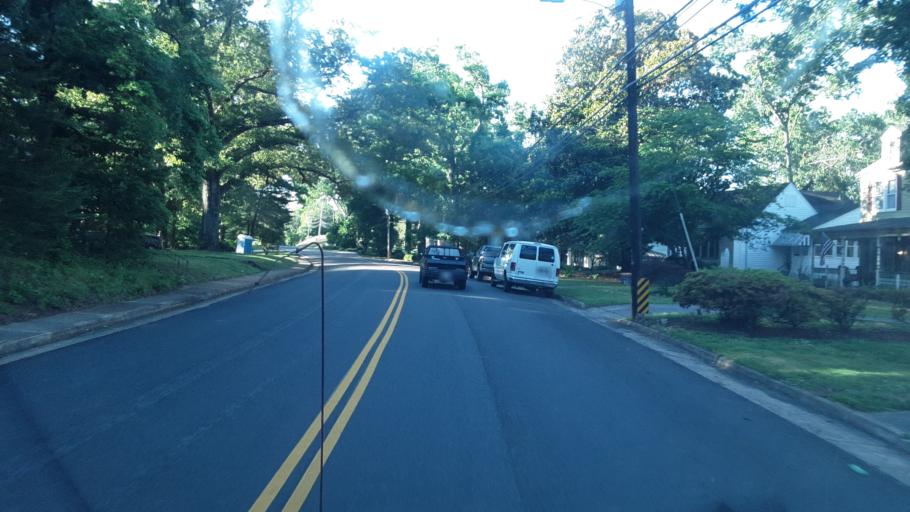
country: US
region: Virginia
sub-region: Pittsylvania County
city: Chatham
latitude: 36.8128
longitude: -79.3947
